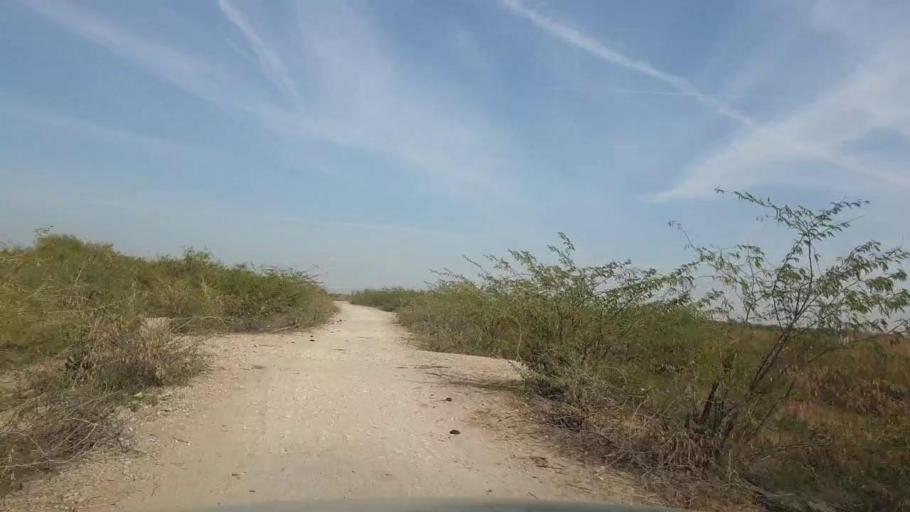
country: PK
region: Sindh
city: Nabisar
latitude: 25.1206
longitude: 69.6380
